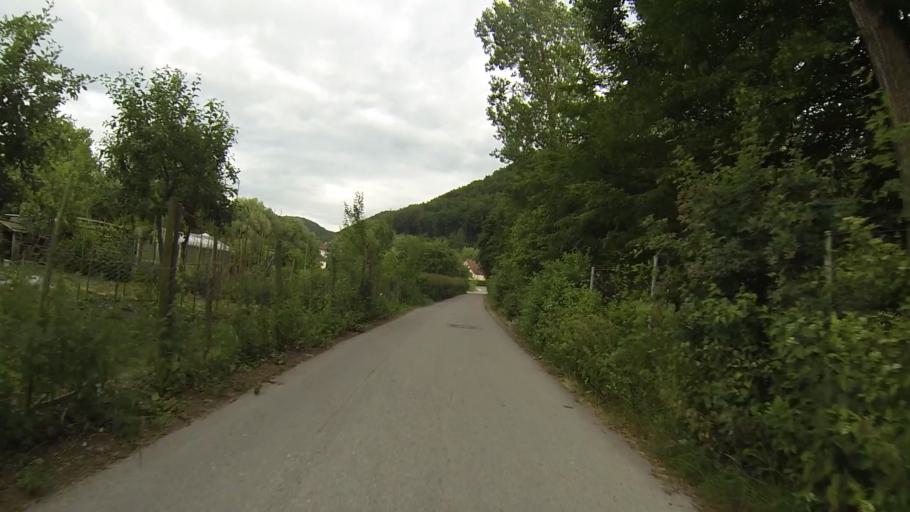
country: DE
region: Baden-Wuerttemberg
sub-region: Tuebingen Region
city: Blaubeuren
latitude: 48.4025
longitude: 9.7976
